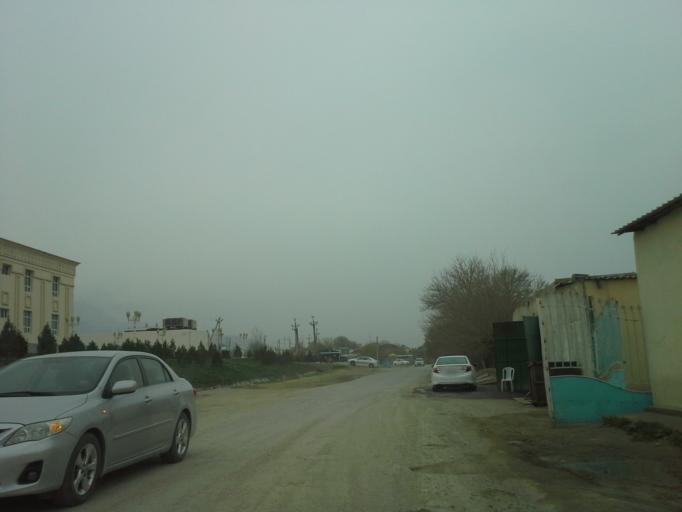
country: TM
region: Ahal
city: Abadan
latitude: 37.9675
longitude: 58.2168
